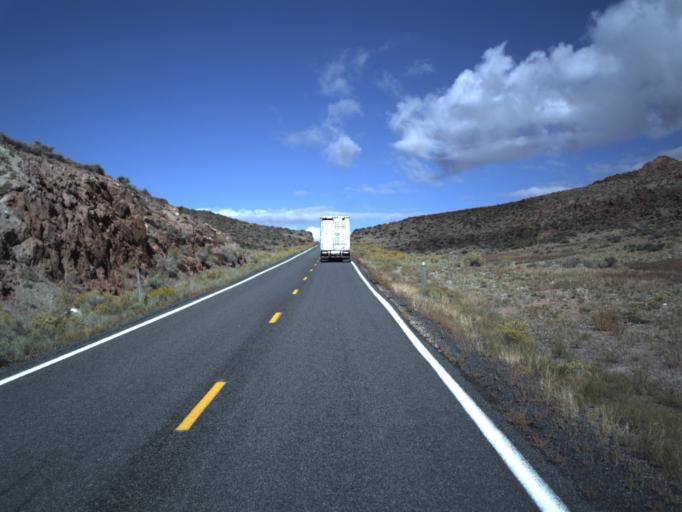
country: US
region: Utah
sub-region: Beaver County
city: Milford
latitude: 38.6136
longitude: -113.8392
